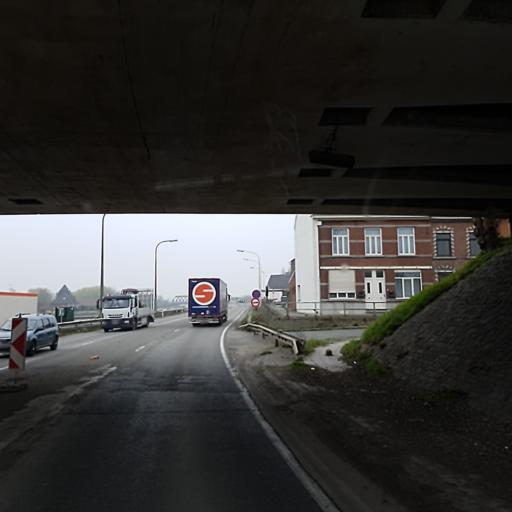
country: BE
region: Wallonia
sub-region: Province du Hainaut
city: Mons
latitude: 50.4791
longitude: 3.9500
